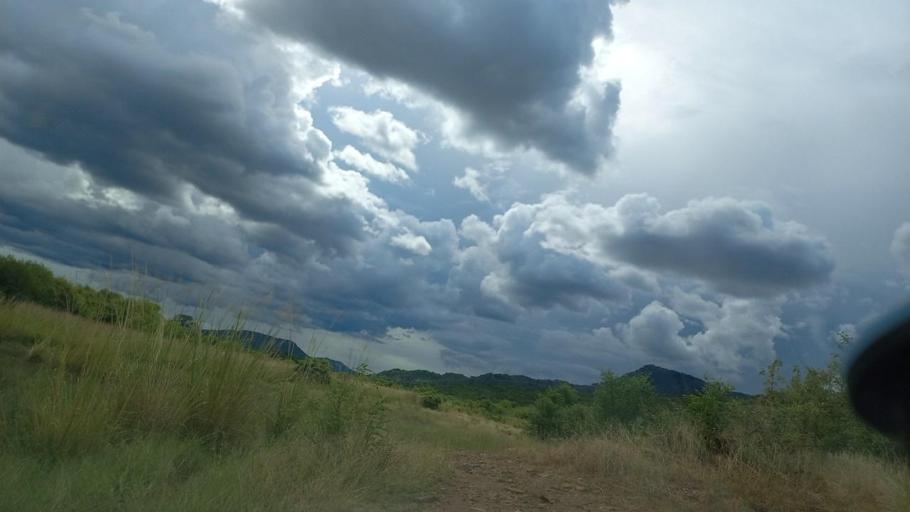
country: ZM
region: Lusaka
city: Luangwa
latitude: -15.6513
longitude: 30.3470
